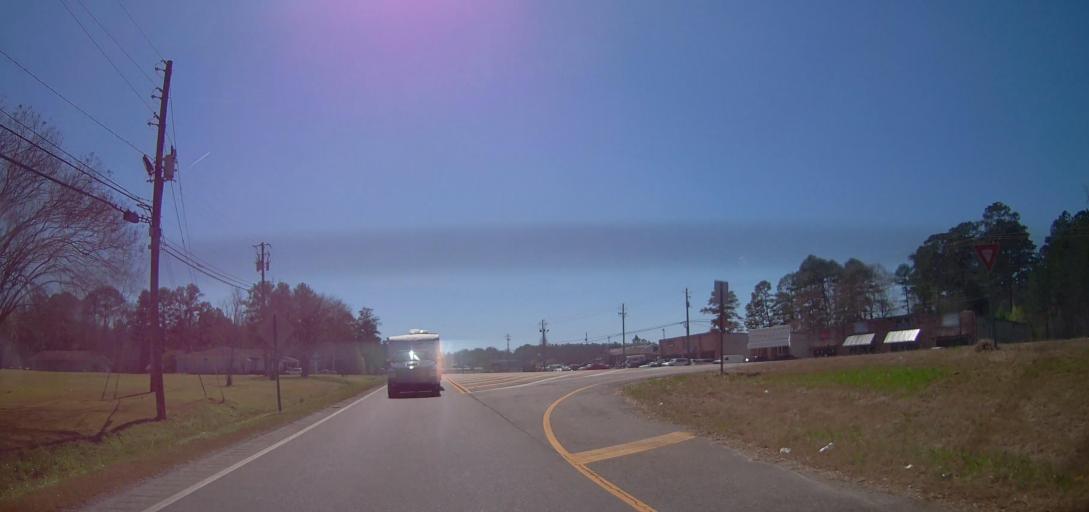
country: US
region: Alabama
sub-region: Etowah County
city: Southside
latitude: 33.9372
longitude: -86.0239
